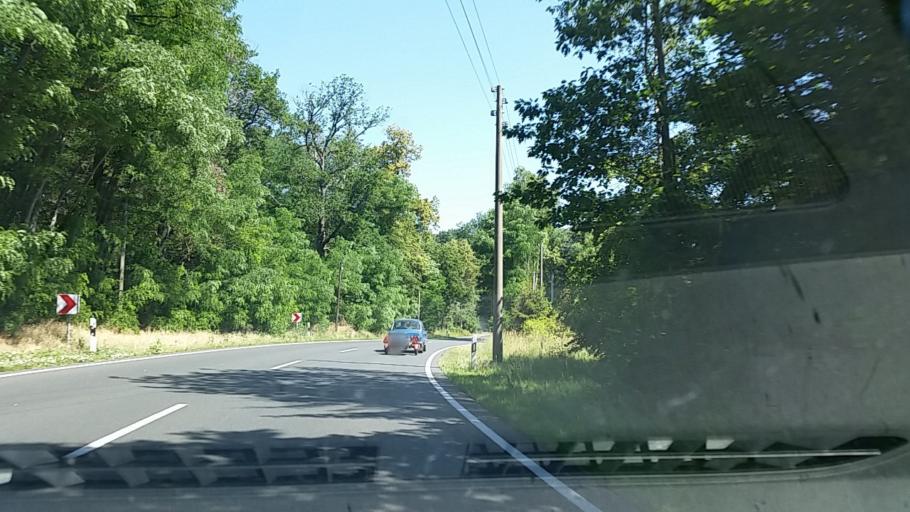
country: DE
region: Saxony-Anhalt
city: Kemberg
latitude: 51.6943
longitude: 12.6140
